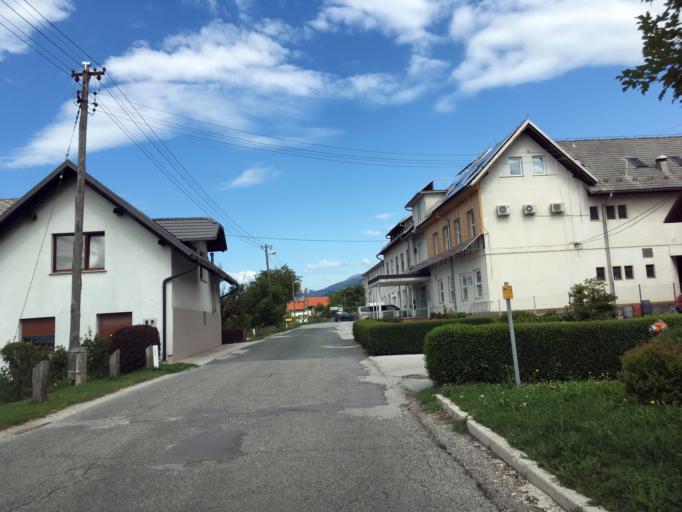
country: SI
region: Zirovnica
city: Zirovnica
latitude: 46.3958
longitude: 14.1523
